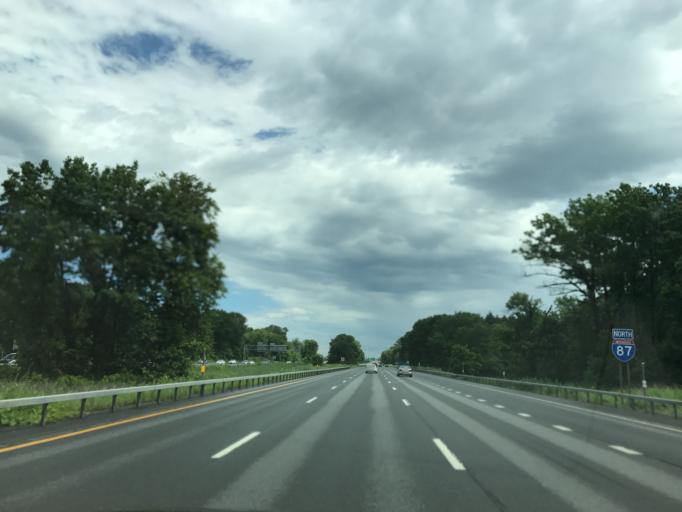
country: US
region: New York
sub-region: Albany County
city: Roessleville
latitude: 42.7443
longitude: -73.7767
